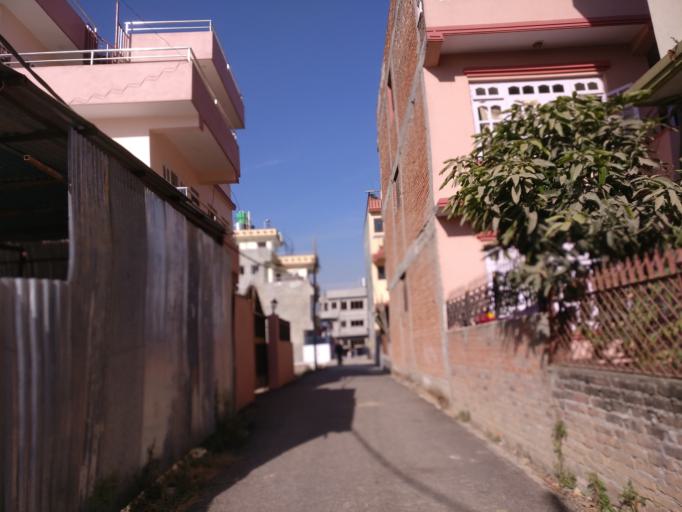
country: NP
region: Central Region
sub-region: Bagmati Zone
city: Patan
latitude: 27.6752
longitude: 85.3352
